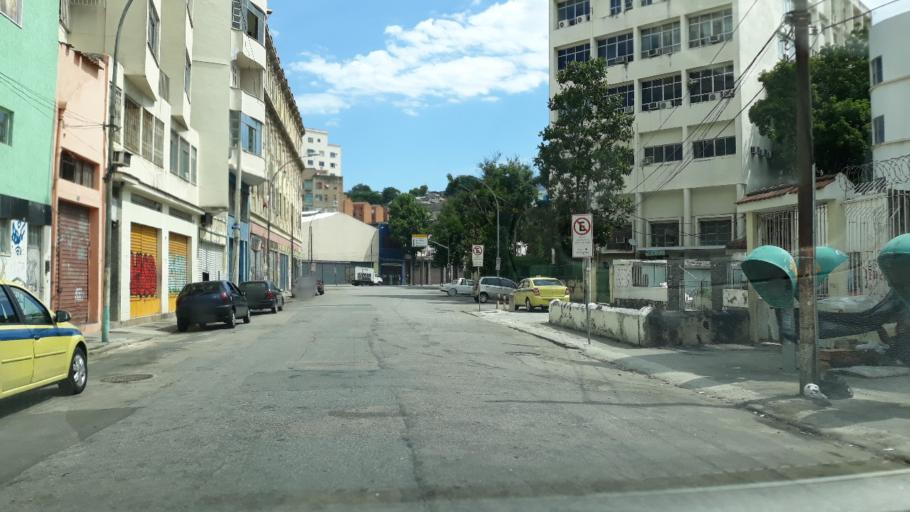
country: BR
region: Rio de Janeiro
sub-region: Rio De Janeiro
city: Rio de Janeiro
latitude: -22.9095
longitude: -43.1920
